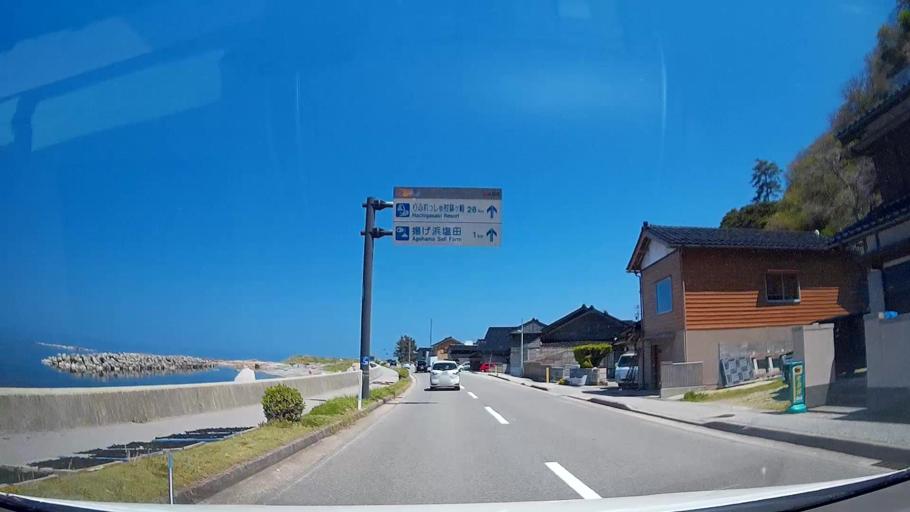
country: JP
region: Ishikawa
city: Nanao
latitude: 37.4812
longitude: 137.1074
